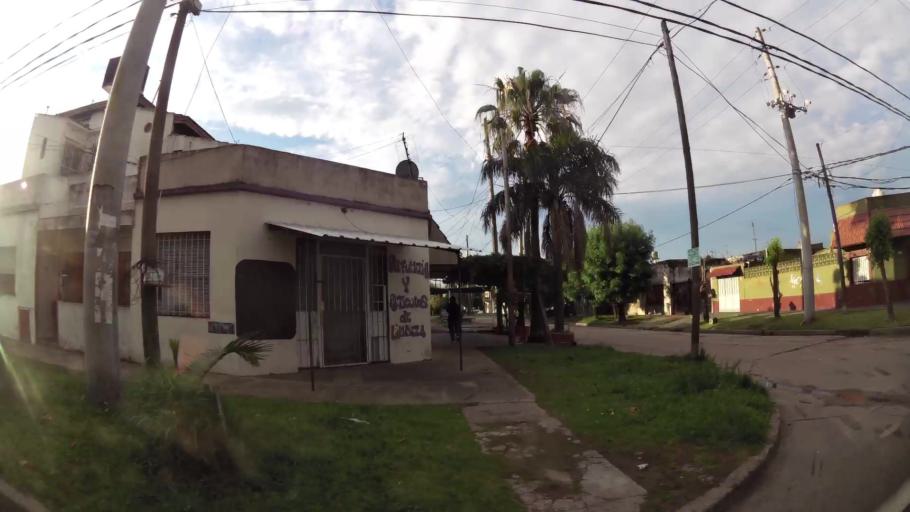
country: AR
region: Buenos Aires
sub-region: Partido de Lomas de Zamora
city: Lomas de Zamora
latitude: -34.7562
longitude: -58.3547
